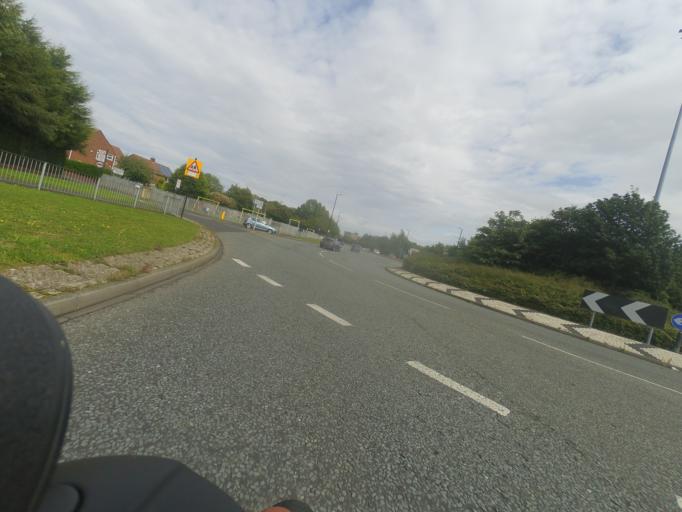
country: GB
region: England
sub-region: South Tyneside
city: Jarrow
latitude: 54.9954
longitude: -1.4745
